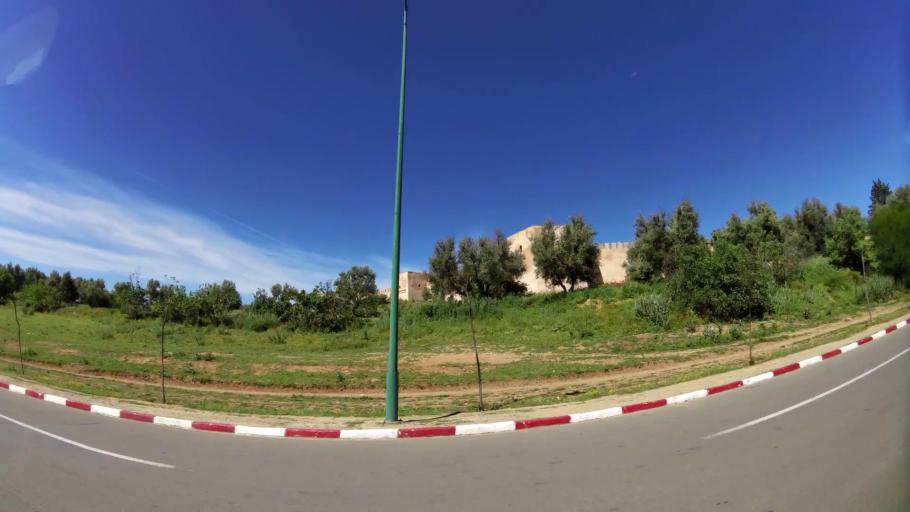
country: MA
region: Meknes-Tafilalet
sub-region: Meknes
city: Meknes
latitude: 33.8760
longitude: -5.5372
